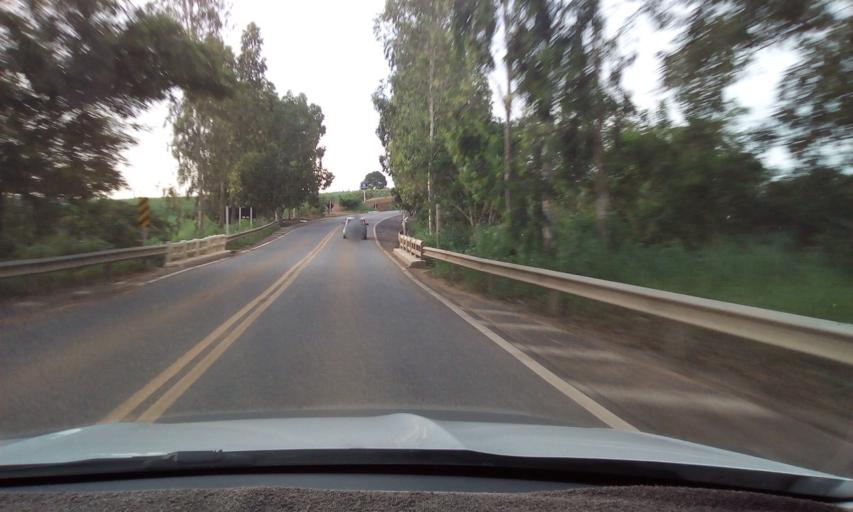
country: BR
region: Pernambuco
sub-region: Vicencia
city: Vicencia
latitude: -7.6145
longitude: -35.2393
